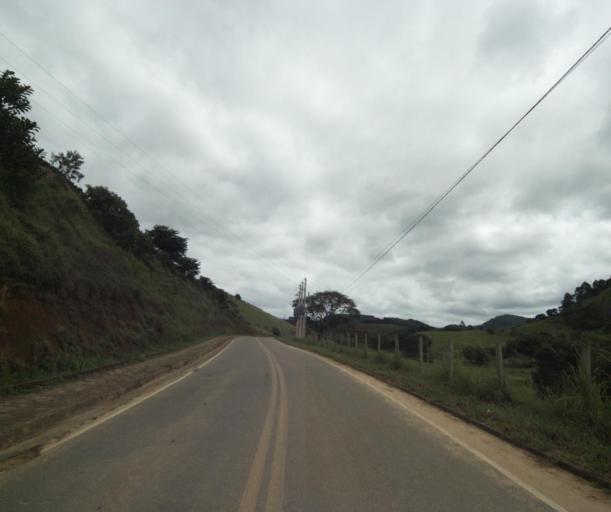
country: BR
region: Espirito Santo
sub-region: Irupi
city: Irupi
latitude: -20.3520
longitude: -41.6299
